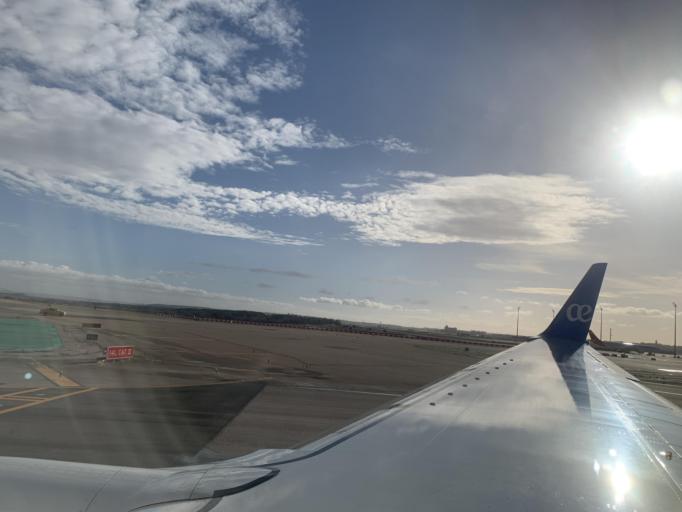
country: ES
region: Madrid
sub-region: Provincia de Madrid
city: Barajas de Madrid
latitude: 40.4956
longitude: -3.5606
